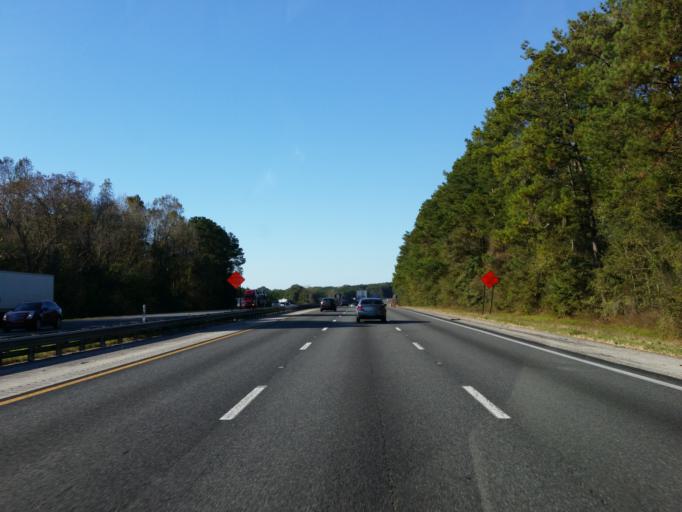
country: US
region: Florida
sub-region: Alachua County
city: Alachua
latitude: 29.7558
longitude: -82.4963
